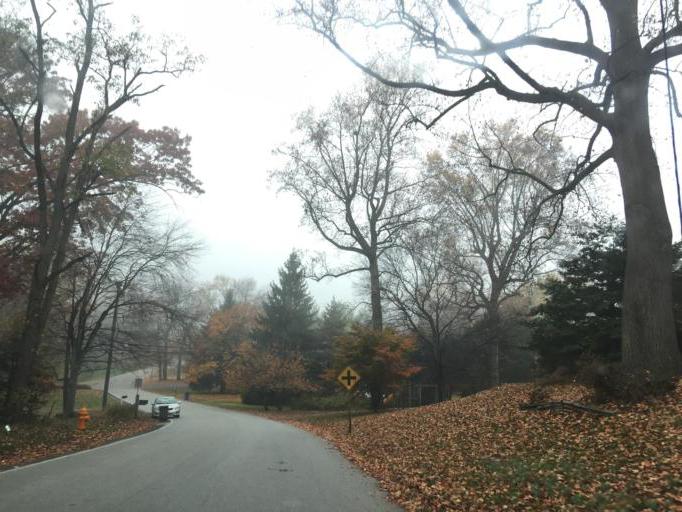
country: US
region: Maryland
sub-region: Howard County
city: Riverside
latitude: 39.1866
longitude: -76.8576
